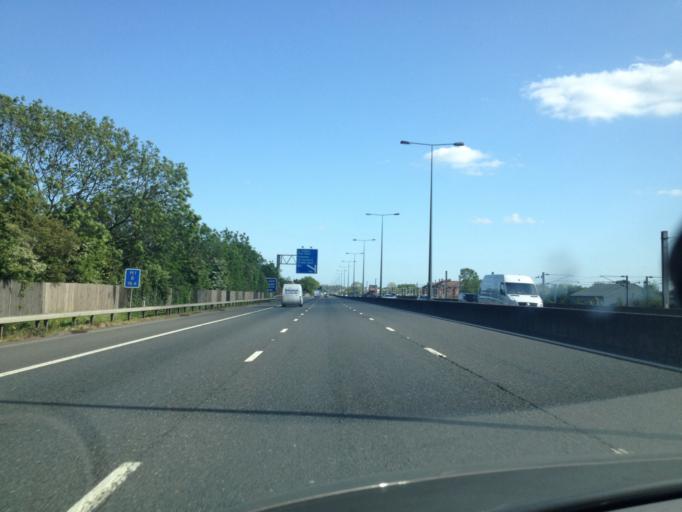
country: GB
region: England
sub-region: Greater London
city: Edgware
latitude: 51.6158
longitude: -0.2512
